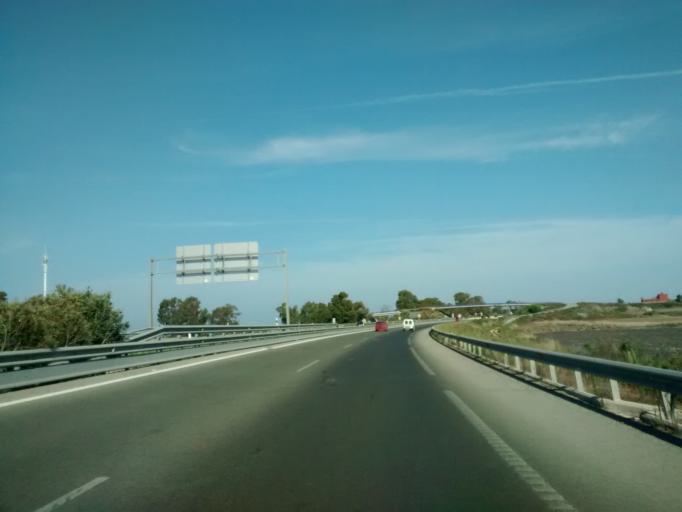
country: ES
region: Andalusia
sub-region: Provincia de Cadiz
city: Chiclana de la Frontera
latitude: 36.3583
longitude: -6.1072
